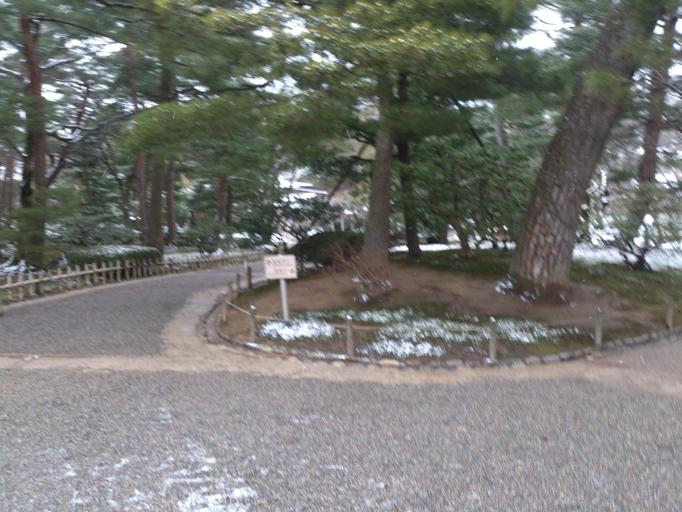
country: JP
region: Ishikawa
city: Kanazawa-shi
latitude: 36.5634
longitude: 136.6627
